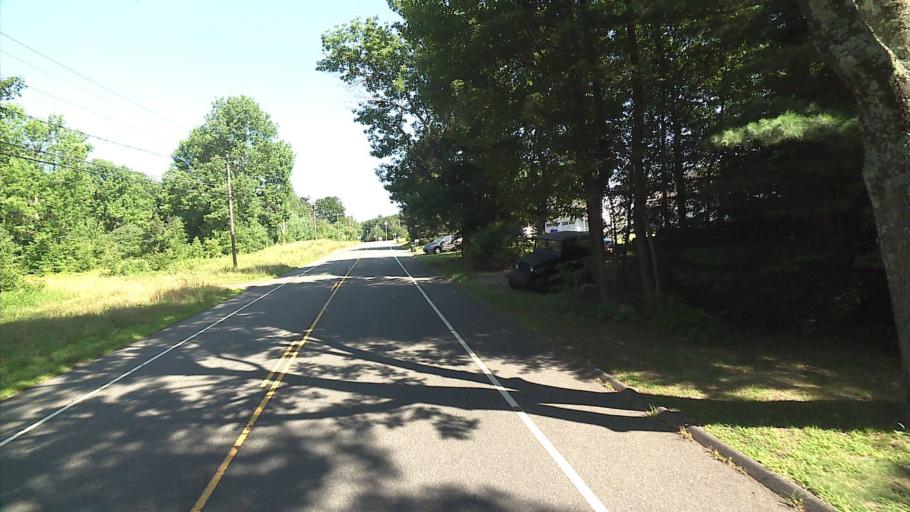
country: US
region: Connecticut
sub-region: Hartford County
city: North Granby
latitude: 41.9923
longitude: -72.8984
